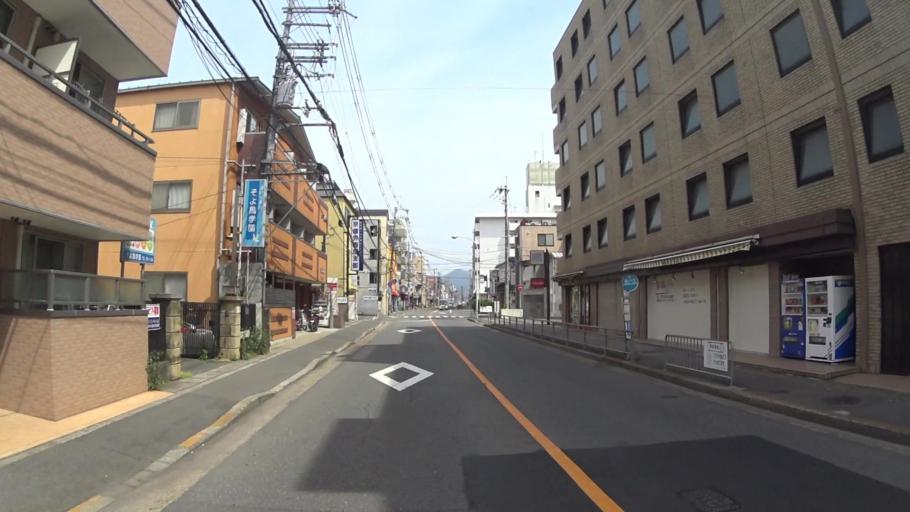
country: JP
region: Kyoto
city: Muko
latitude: 34.9836
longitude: 135.6931
